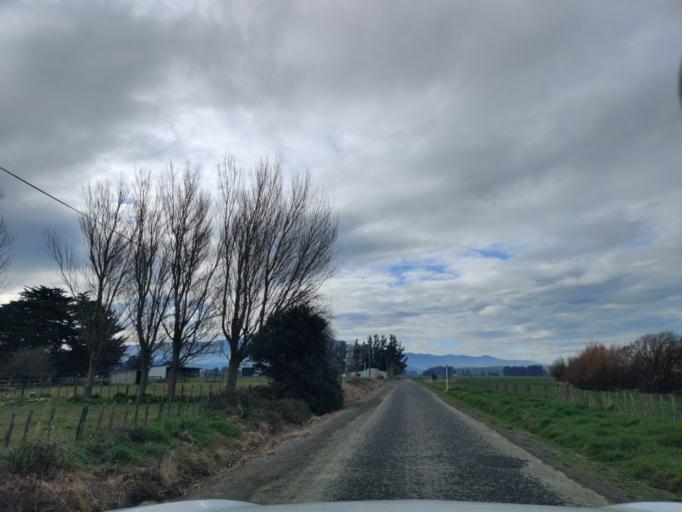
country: NZ
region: Manawatu-Wanganui
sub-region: Palmerston North City
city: Palmerston North
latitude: -40.3334
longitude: 175.8563
